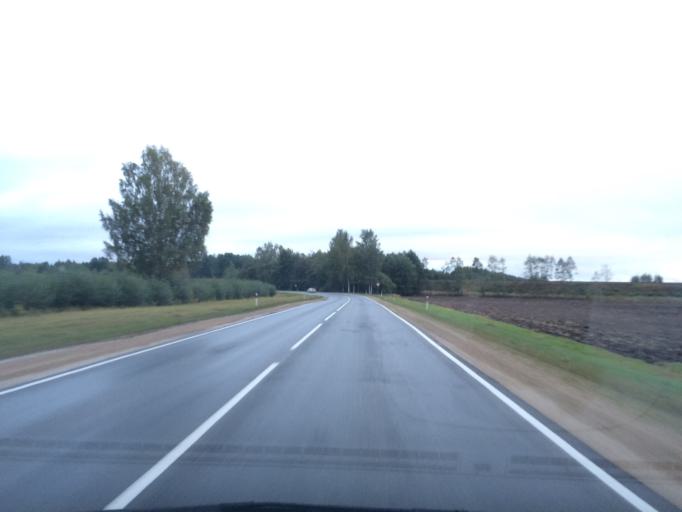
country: LV
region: Salas
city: Sala
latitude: 56.5512
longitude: 25.7964
